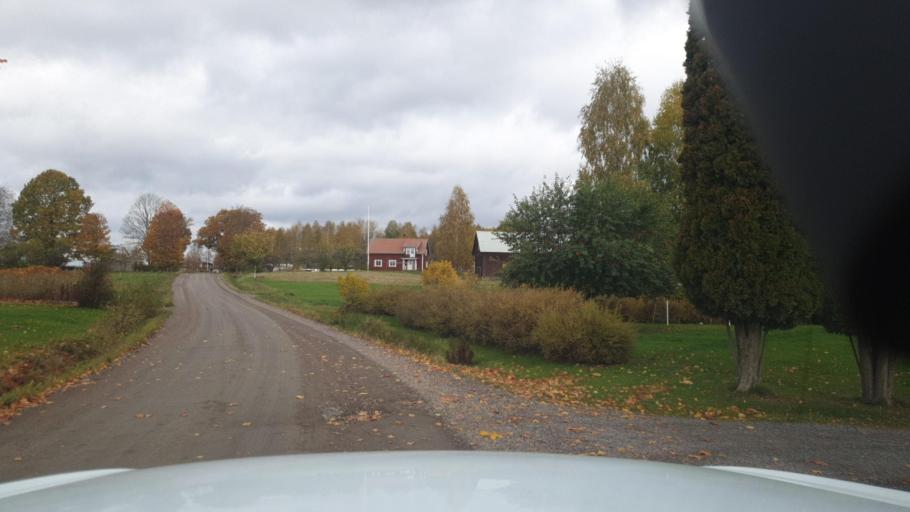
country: SE
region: Vaermland
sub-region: Sunne Kommun
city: Sunne
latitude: 59.7976
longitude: 13.1079
